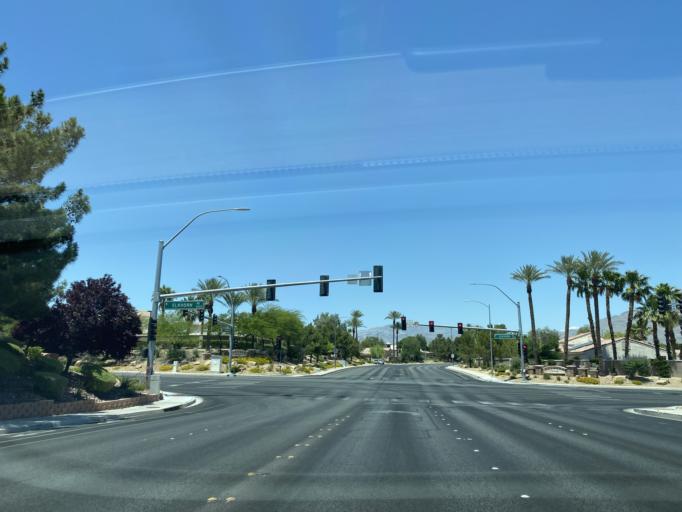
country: US
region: Nevada
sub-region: Clark County
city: Las Vegas
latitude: 36.2907
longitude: -115.2694
